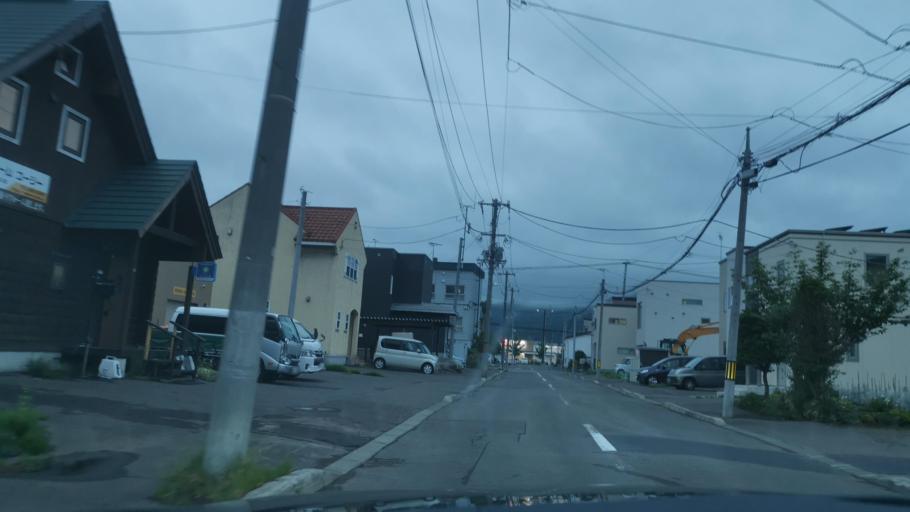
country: JP
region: Hokkaido
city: Sapporo
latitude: 43.1083
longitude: 141.2748
